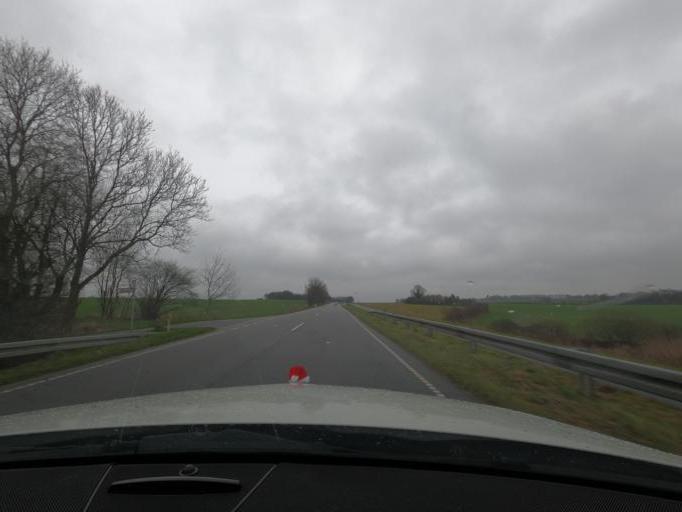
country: DK
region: South Denmark
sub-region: Haderslev Kommune
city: Starup
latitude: 55.2490
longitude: 9.5848
